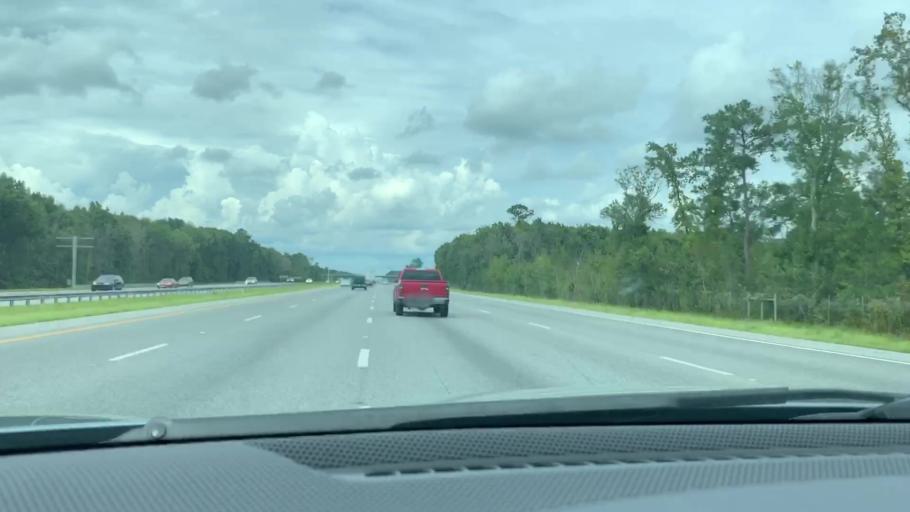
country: US
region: Georgia
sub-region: McIntosh County
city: Darien
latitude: 31.4856
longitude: -81.4469
